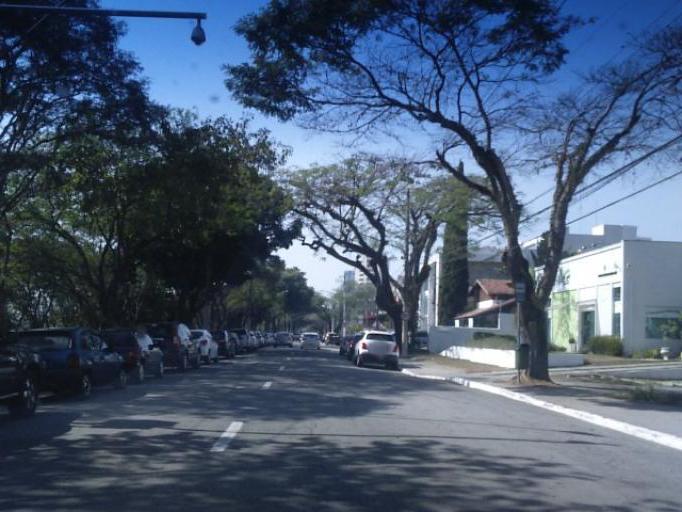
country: BR
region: Sao Paulo
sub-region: Sao Jose Dos Campos
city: Sao Jose dos Campos
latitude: -23.1928
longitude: -45.8984
